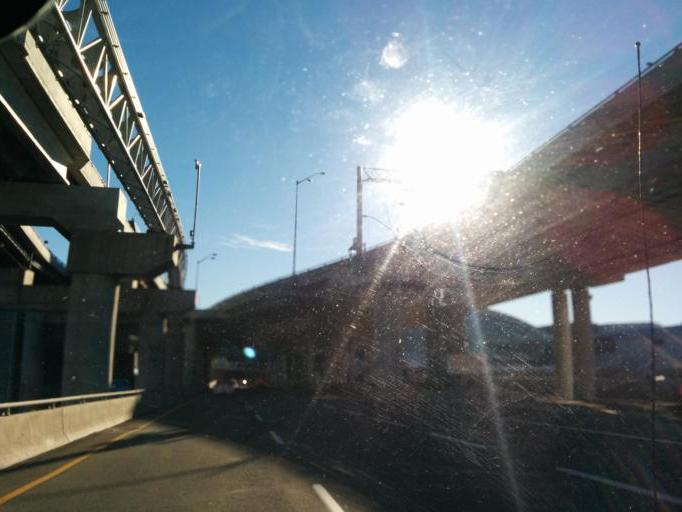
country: CA
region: Ontario
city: Etobicoke
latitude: 43.6840
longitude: -79.6150
